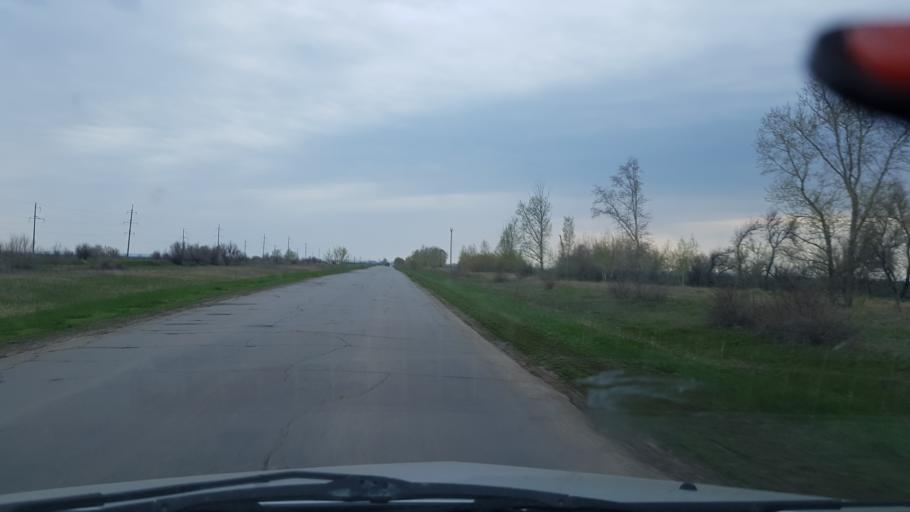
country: RU
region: Samara
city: Khryashchevka
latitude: 53.6686
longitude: 49.1353
